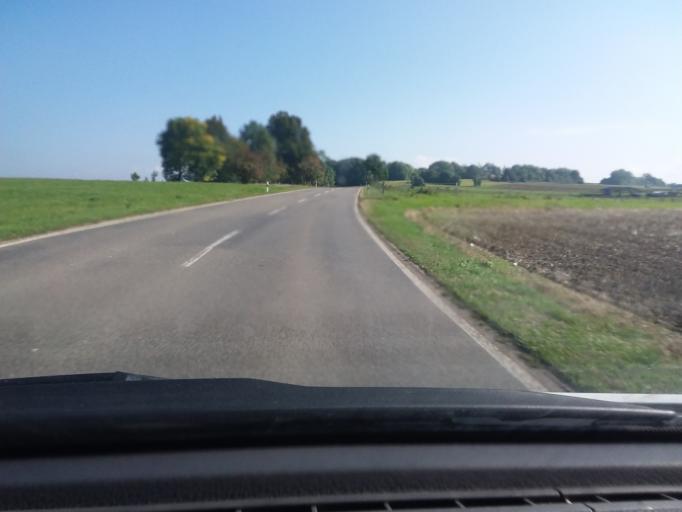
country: DE
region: Baden-Wuerttemberg
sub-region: Regierungsbezirk Stuttgart
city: Bad Uberkingen
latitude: 48.5925
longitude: 9.8116
